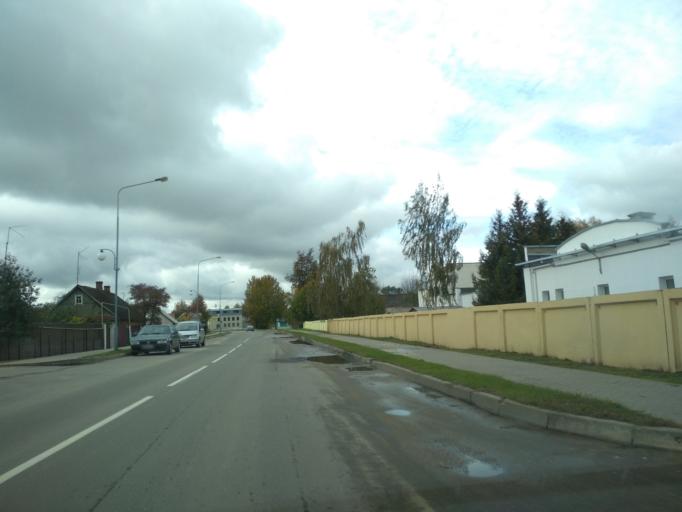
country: BY
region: Minsk
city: Mar''ina Horka
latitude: 53.5194
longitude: 28.1520
